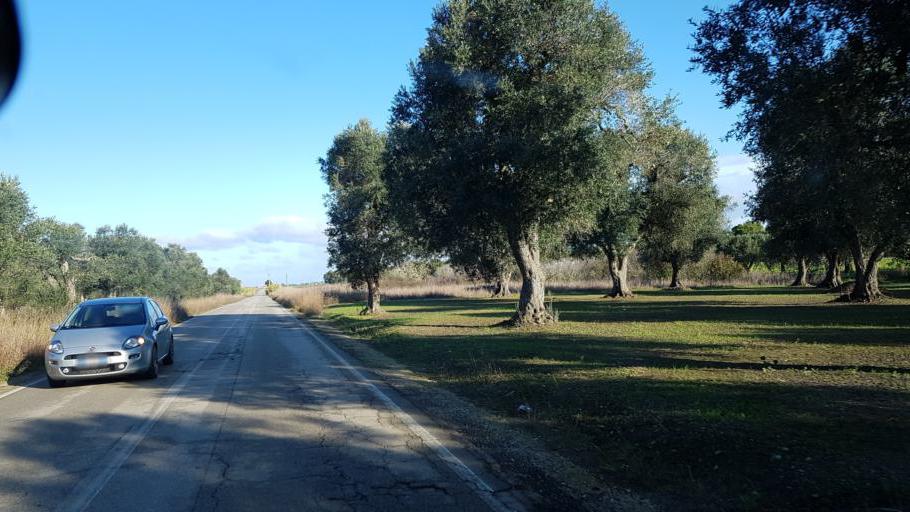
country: IT
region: Apulia
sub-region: Provincia di Brindisi
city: Tuturano
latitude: 40.5660
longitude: 17.9491
